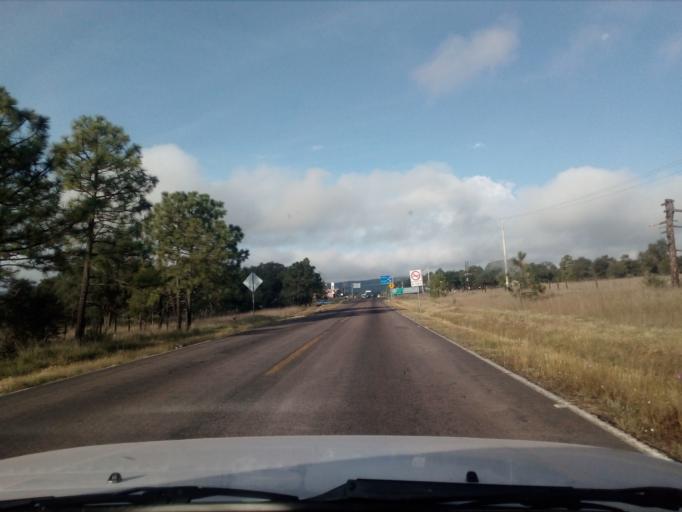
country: MX
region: Durango
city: Victoria de Durango
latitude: 23.9257
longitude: -104.9376
